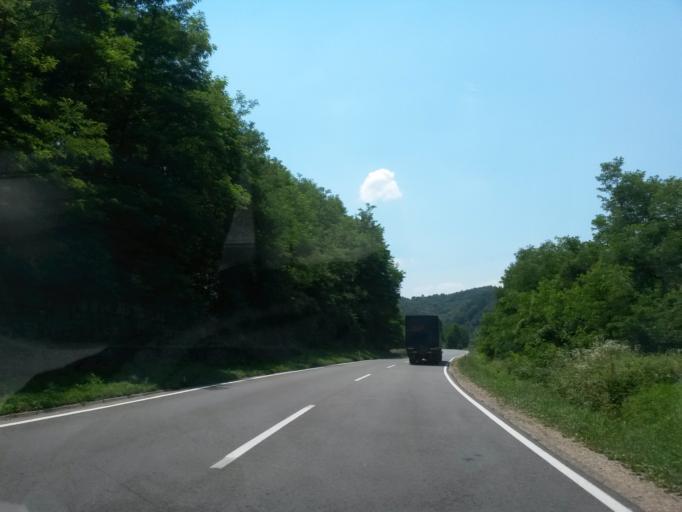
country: BA
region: Federation of Bosnia and Herzegovina
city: Lijesnica
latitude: 44.5069
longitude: 18.0817
